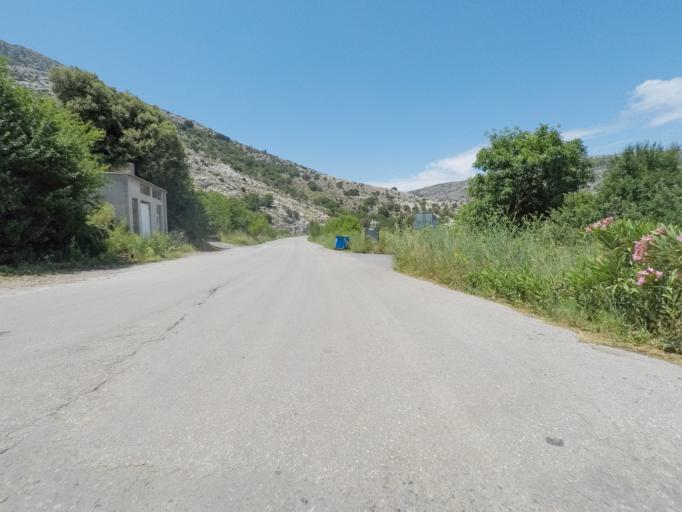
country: GR
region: Crete
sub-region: Nomos Irakleiou
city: Mokhos
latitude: 35.1858
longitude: 25.4323
